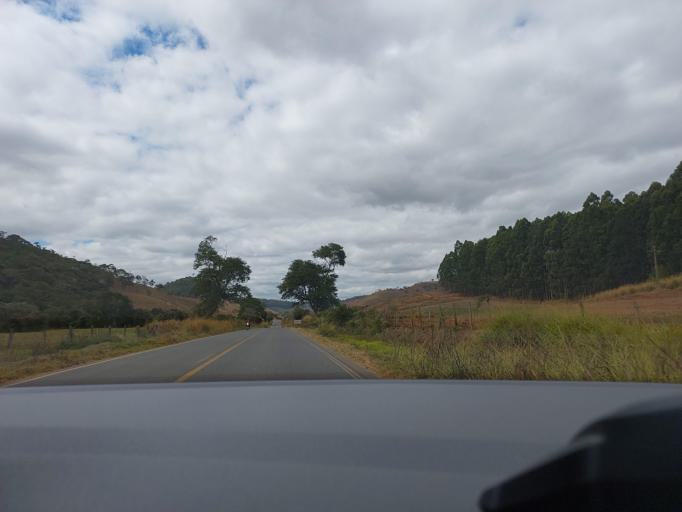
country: BR
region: Minas Gerais
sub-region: Vicosa
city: Vicosa
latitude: -20.8291
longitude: -42.7639
